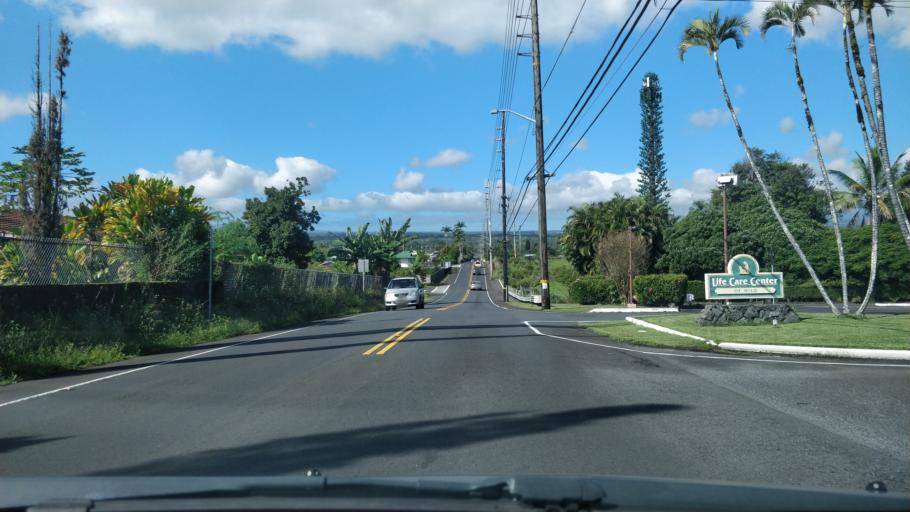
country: US
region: Hawaii
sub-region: Hawaii County
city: Hilo
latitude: 19.6828
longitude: -155.0945
